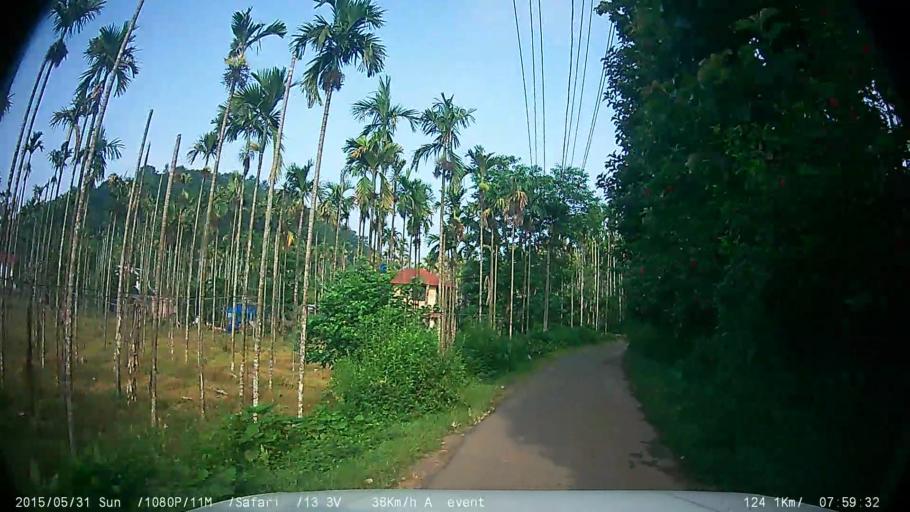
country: IN
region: Kerala
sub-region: Wayanad
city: Kalpetta
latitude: 11.6337
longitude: 76.0563
